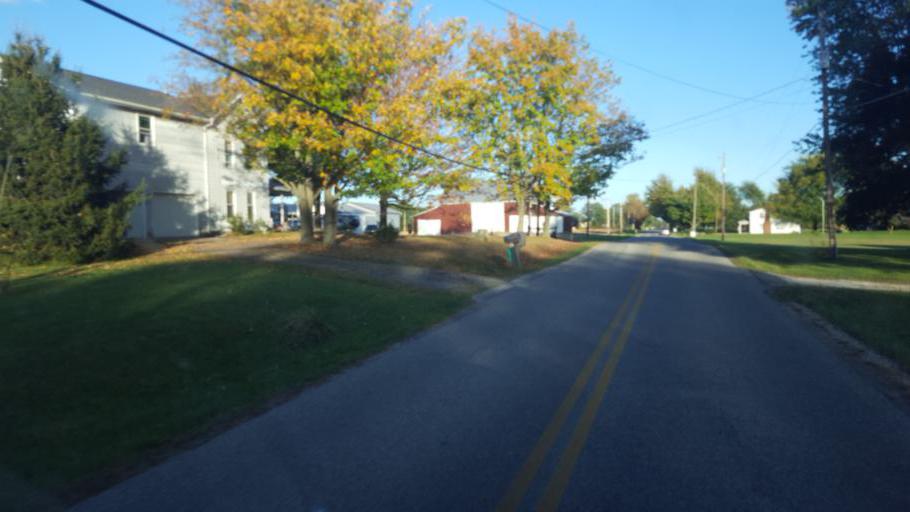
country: US
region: Ohio
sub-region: Licking County
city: Pataskala
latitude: 40.0152
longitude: -82.7465
